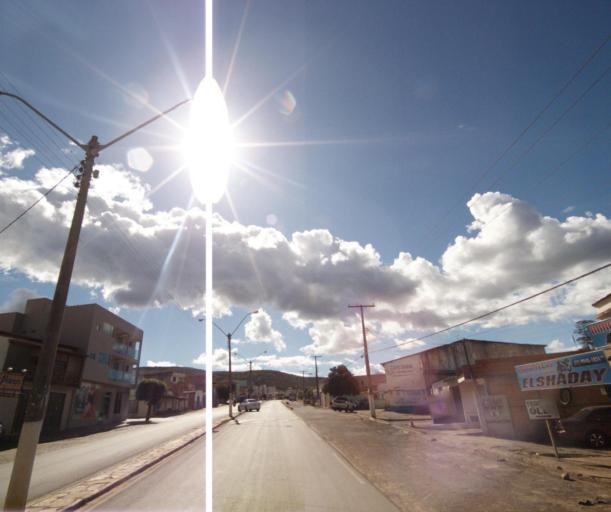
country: BR
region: Bahia
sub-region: Caetite
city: Caetite
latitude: -14.0648
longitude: -42.4915
